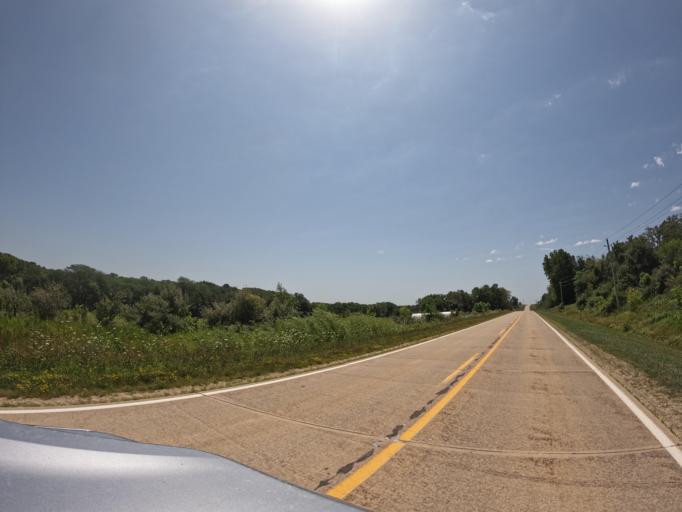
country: US
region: Iowa
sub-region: Henry County
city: Mount Pleasant
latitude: 40.9412
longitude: -91.5545
